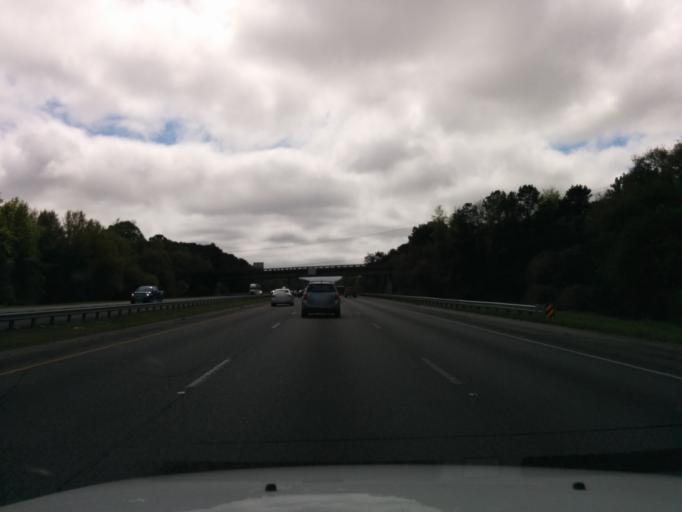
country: US
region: Georgia
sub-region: Chatham County
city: Georgetown
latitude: 32.0440
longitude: -81.2614
